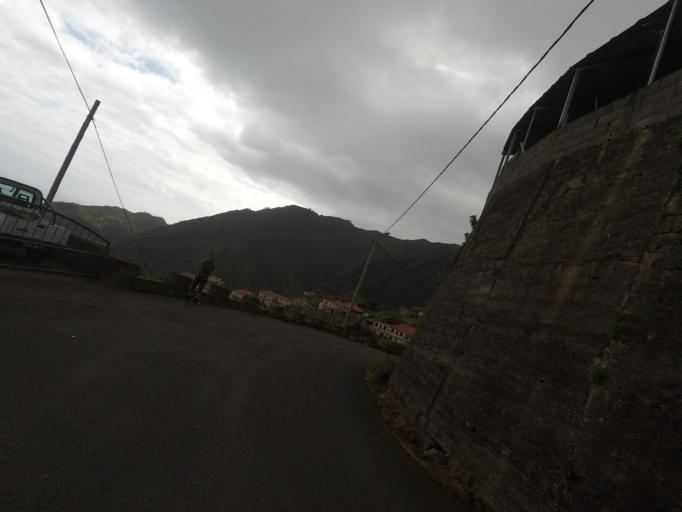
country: PT
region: Madeira
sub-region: Santana
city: Santana
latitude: 32.7537
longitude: -16.8269
